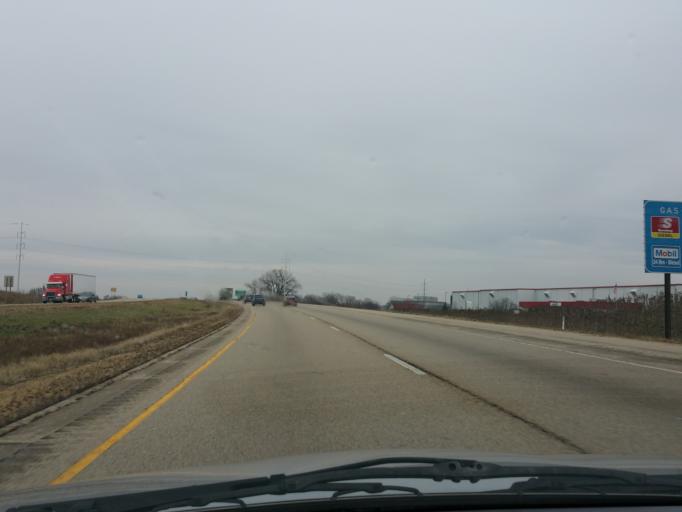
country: US
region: Wisconsin
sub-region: Rock County
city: Beloit
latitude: 42.5173
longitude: -88.9756
